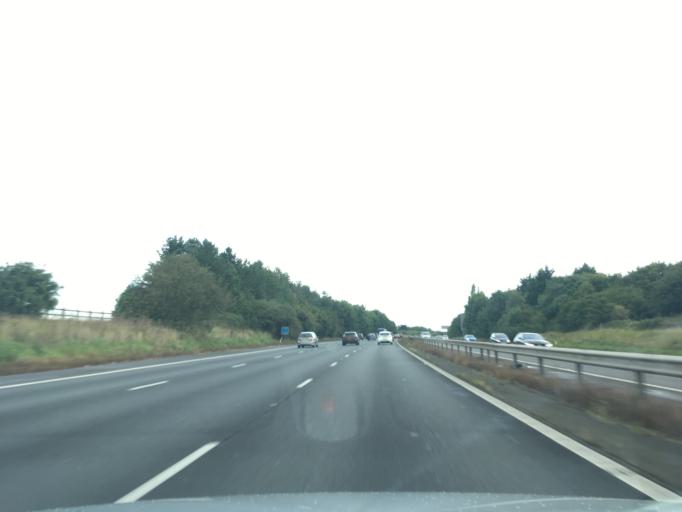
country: GB
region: England
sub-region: Oxfordshire
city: Bicester
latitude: 51.8871
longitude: -1.2051
